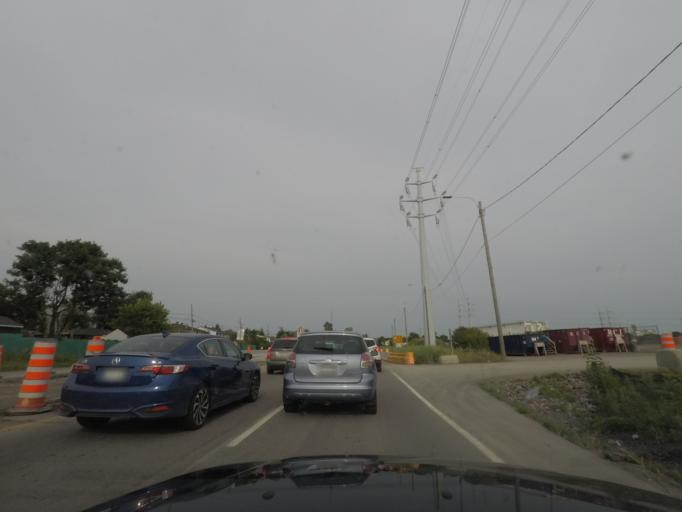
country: CA
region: Quebec
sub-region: Monteregie
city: Brossard
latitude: 45.4677
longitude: -73.4894
